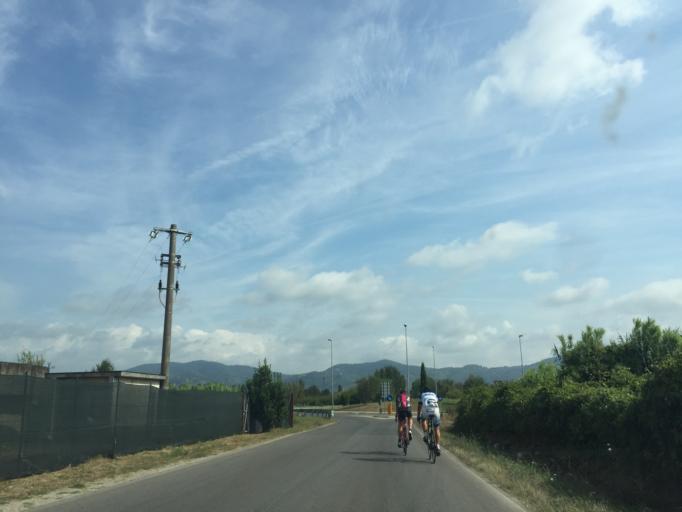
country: IT
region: Tuscany
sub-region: Provincia di Pistoia
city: San Rocco
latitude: 43.8135
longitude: 10.8503
